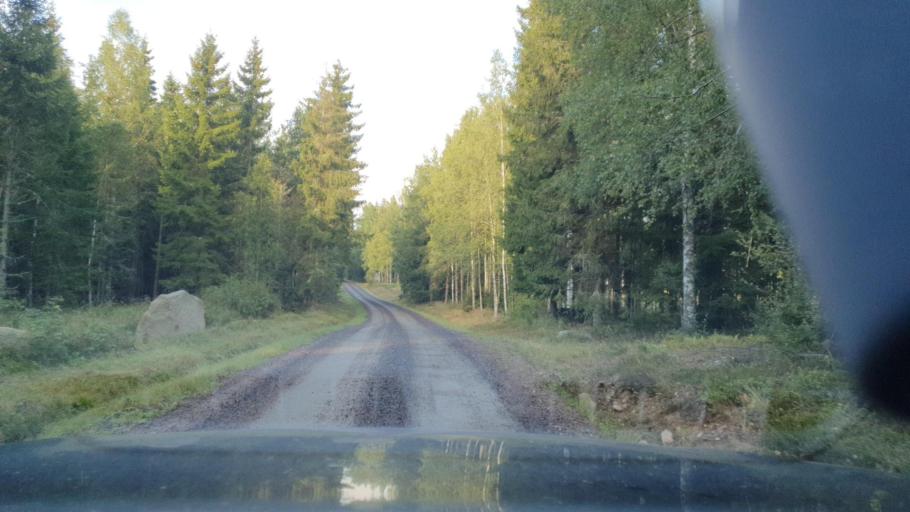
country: SE
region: Vaermland
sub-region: Kristinehamns Kommun
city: Bjorneborg
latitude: 59.1682
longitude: 14.1525
